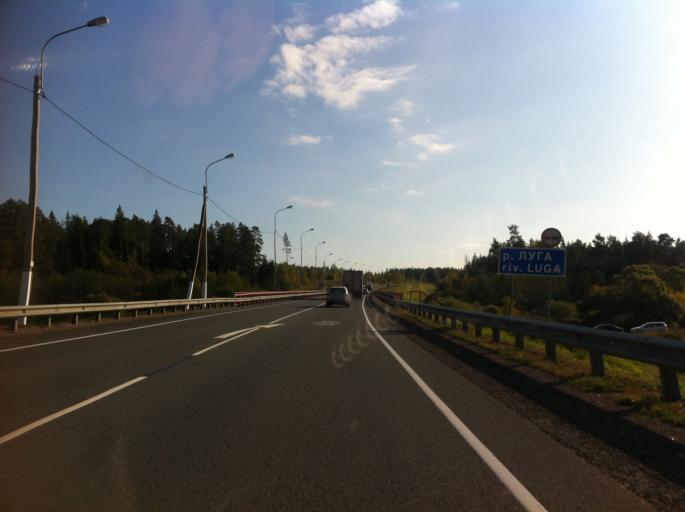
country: RU
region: Leningrad
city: Luga
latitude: 58.7534
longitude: 29.8919
